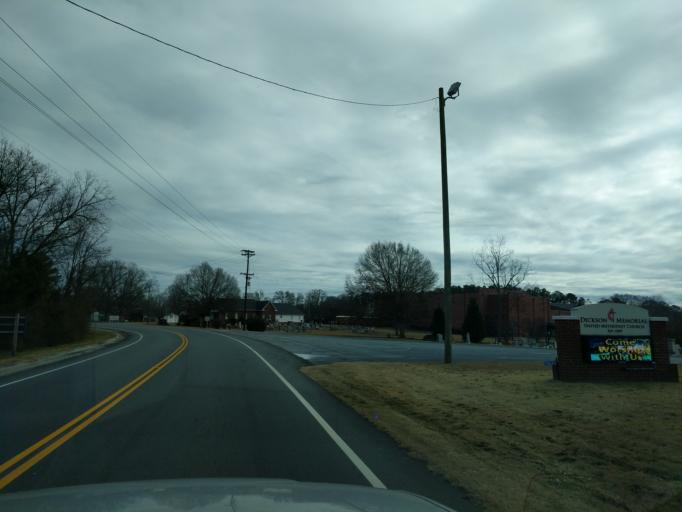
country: US
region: South Carolina
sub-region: Oconee County
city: Utica
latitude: 34.5662
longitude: -82.9049
